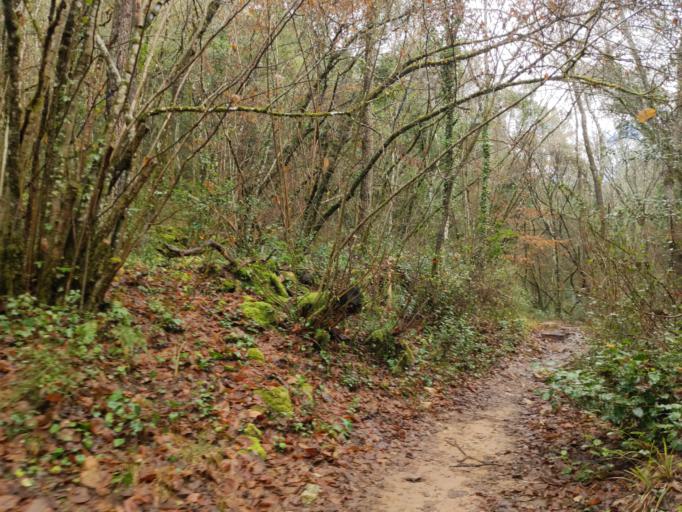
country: FR
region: Provence-Alpes-Cote d'Azur
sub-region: Departement du Var
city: Bagnols-en-Foret
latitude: 43.5408
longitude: 6.7013
